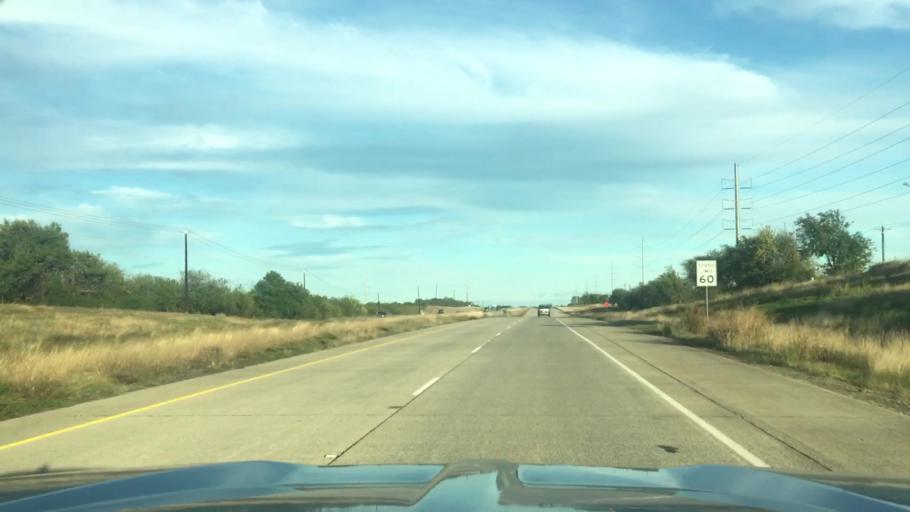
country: US
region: Texas
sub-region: Denton County
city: Denton
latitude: 33.2579
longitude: -97.1571
